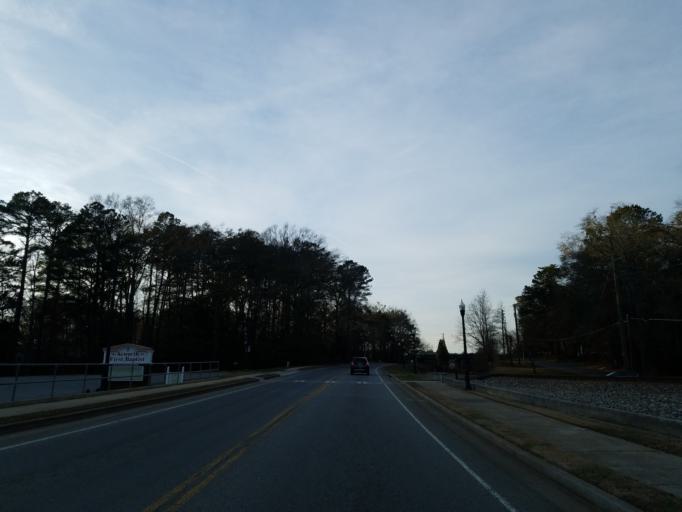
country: US
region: Georgia
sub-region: Cobb County
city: Acworth
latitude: 34.0673
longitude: -84.6835
